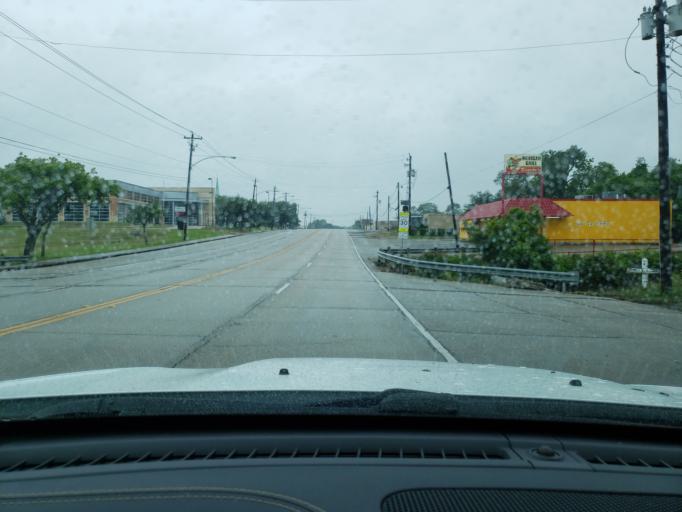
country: US
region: Texas
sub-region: Harris County
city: Baytown
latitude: 29.7340
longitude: -94.9806
